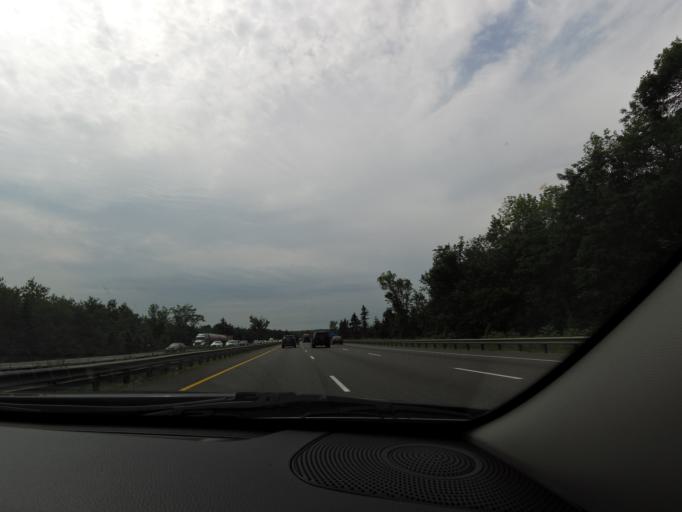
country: CA
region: Ontario
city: Bradford West Gwillimbury
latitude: 44.1837
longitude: -79.6461
